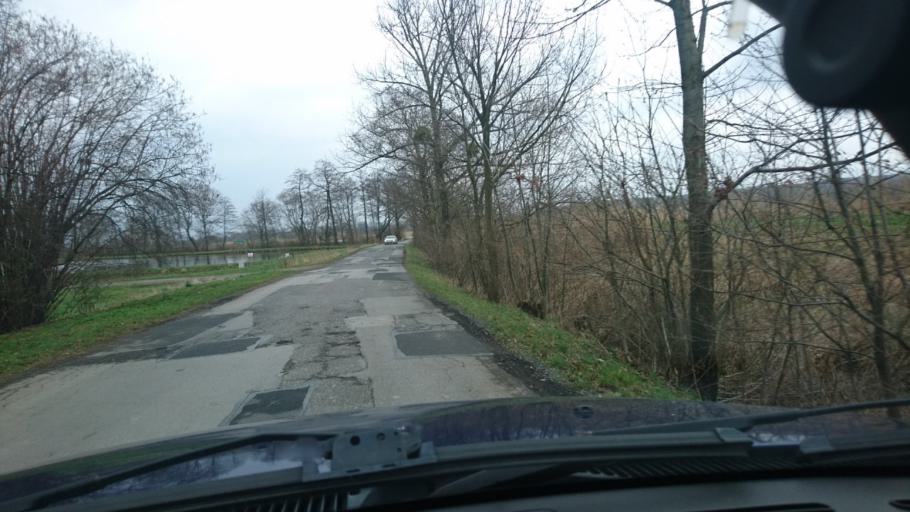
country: PL
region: Silesian Voivodeship
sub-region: Powiat bielski
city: Bronow
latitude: 49.8774
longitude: 18.8882
